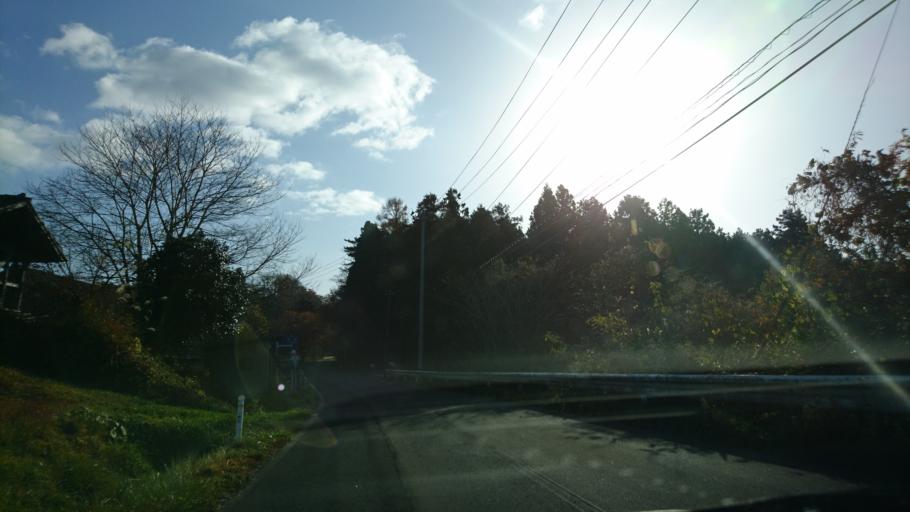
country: JP
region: Iwate
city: Ichinoseki
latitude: 38.8749
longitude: 141.2942
